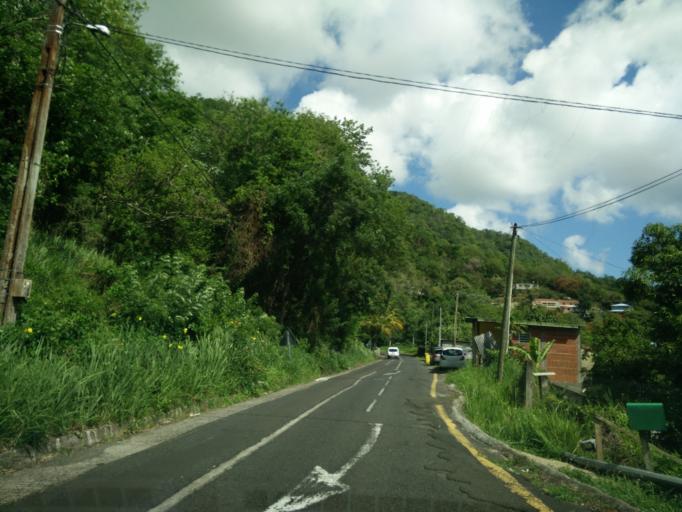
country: MQ
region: Martinique
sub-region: Martinique
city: Les Trois-Ilets
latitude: 14.5208
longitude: -61.0747
